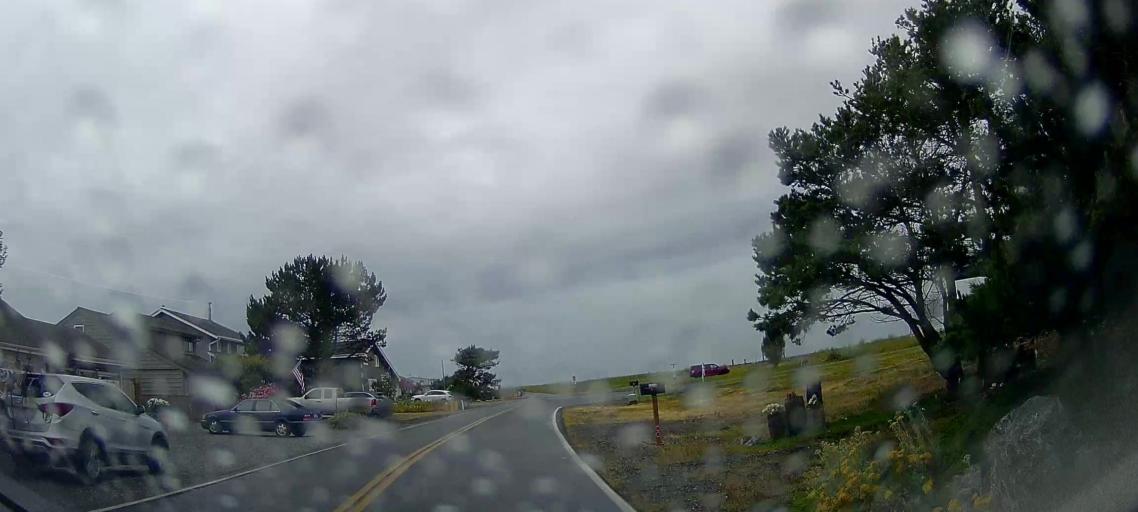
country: US
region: Washington
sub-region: Whatcom County
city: Marietta
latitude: 48.7874
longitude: -122.7039
